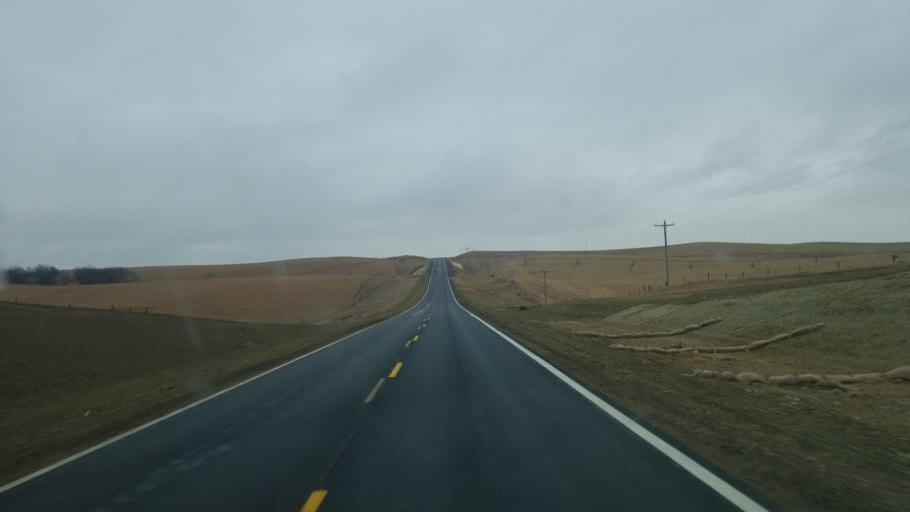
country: US
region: Nebraska
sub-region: Knox County
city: Center
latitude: 42.5970
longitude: -97.7882
